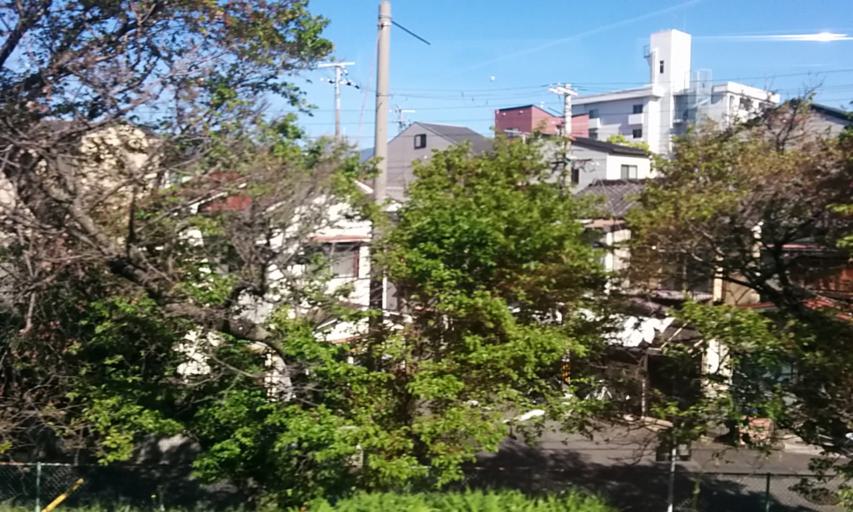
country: JP
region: Kyoto
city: Muko
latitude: 34.9938
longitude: 135.7205
